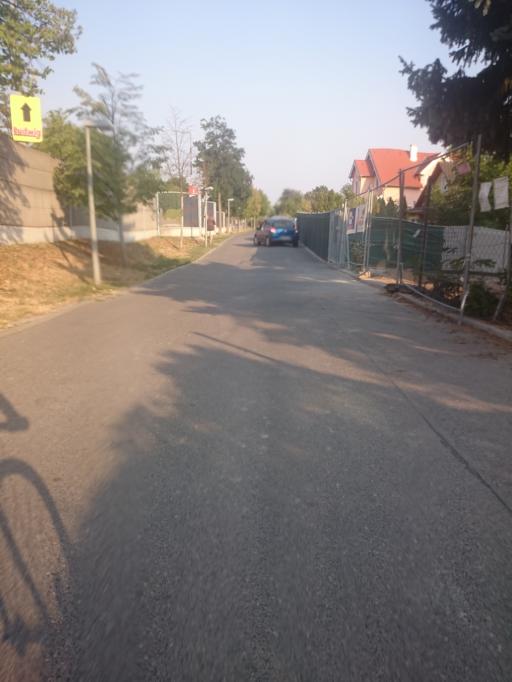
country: AT
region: Lower Austria
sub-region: Politischer Bezirk Wien-Umgebung
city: Gerasdorf bei Wien
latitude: 48.2563
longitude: 16.4215
